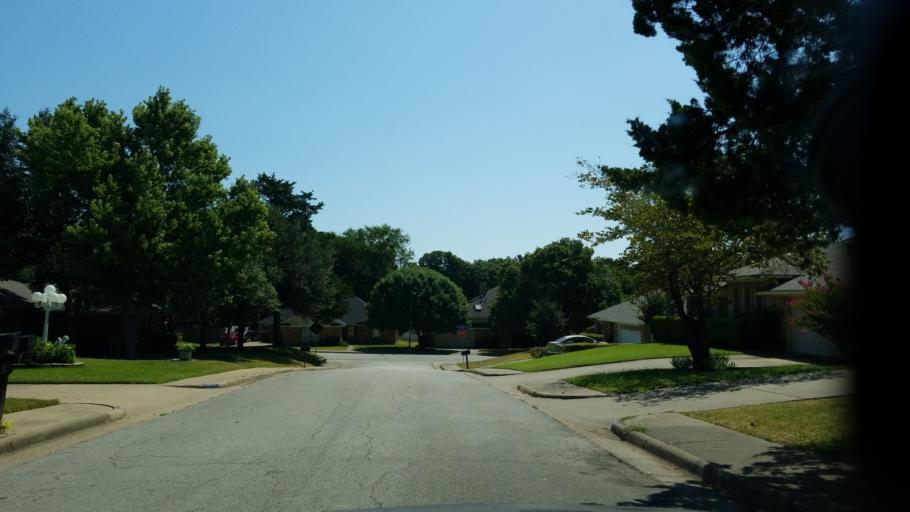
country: US
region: Texas
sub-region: Dallas County
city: Duncanville
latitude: 32.6430
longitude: -96.8948
